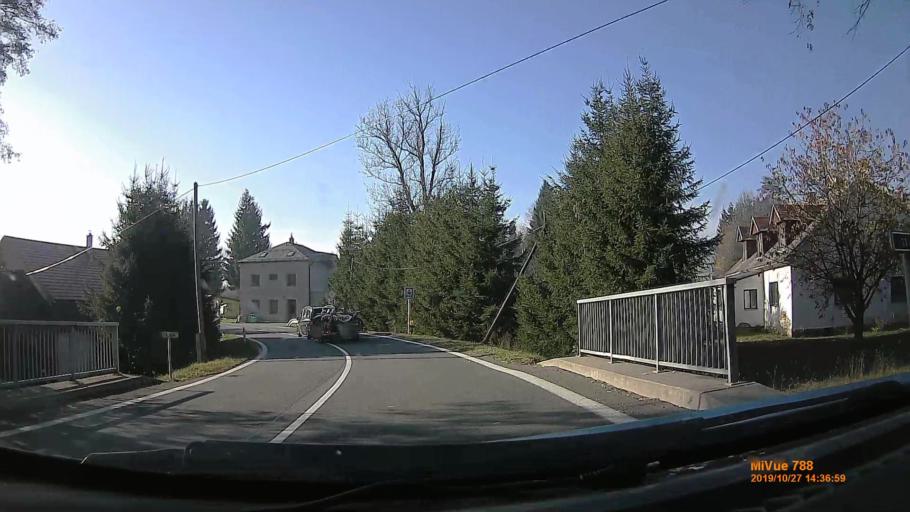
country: CZ
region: Olomoucky
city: Stity
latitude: 49.9899
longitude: 16.7920
